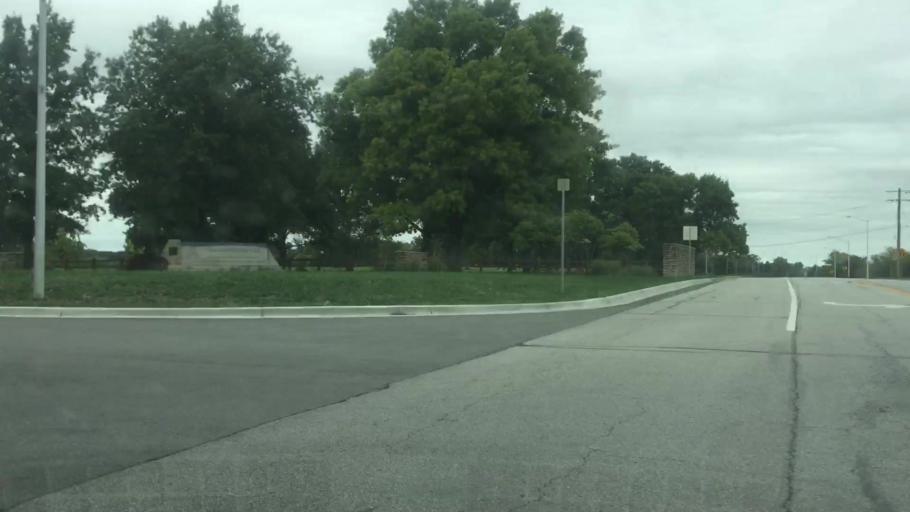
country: US
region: Kansas
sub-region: Johnson County
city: Lenexa
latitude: 38.9856
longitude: -94.7798
